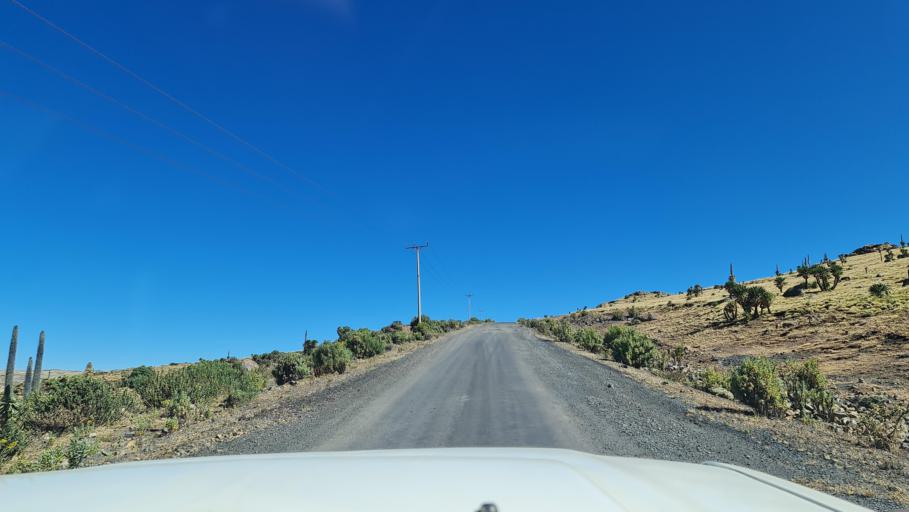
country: ET
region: Amhara
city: Debark'
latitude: 13.1662
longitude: 38.1954
